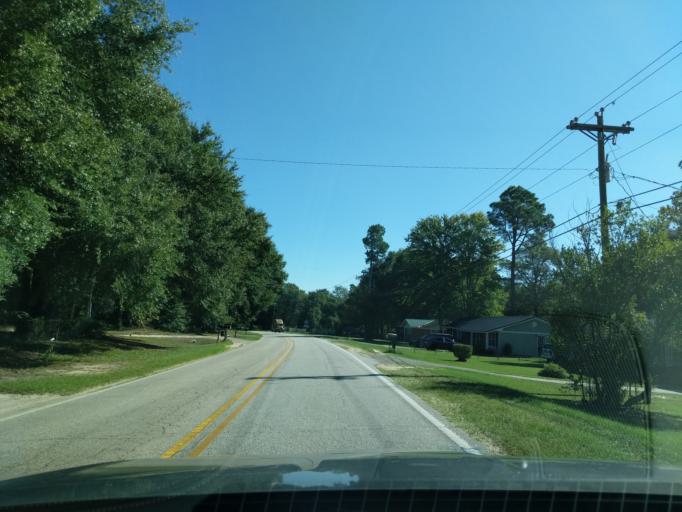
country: US
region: Georgia
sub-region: Richmond County
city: Hephzibah
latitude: 33.2566
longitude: -82.0057
